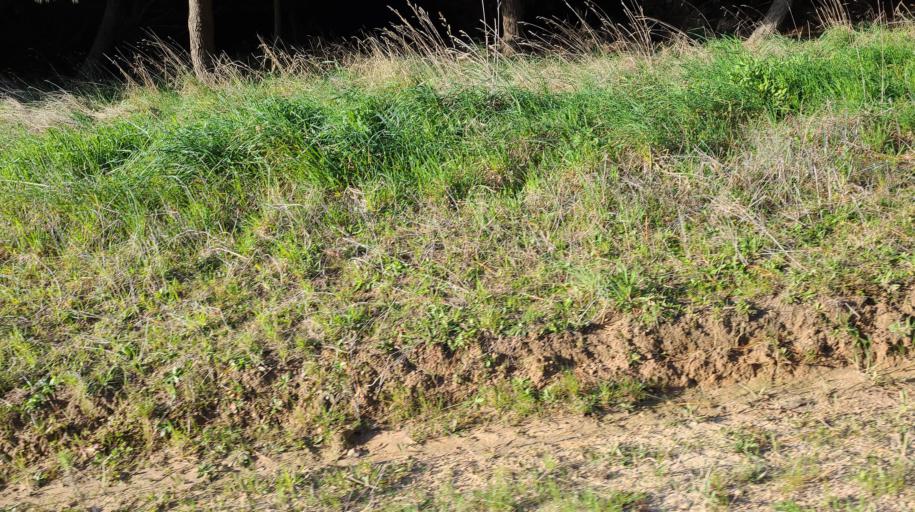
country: AU
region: New South Wales
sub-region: Blayney
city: Millthorpe
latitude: -33.4099
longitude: 149.3073
